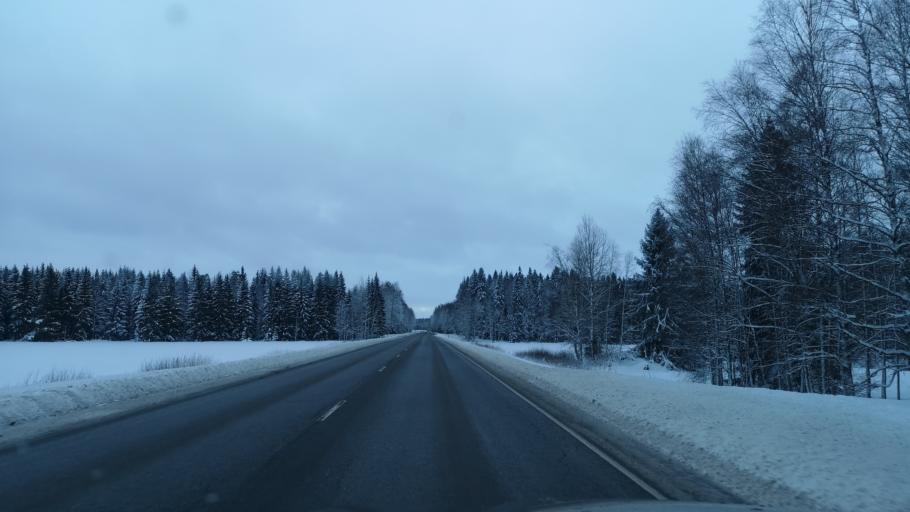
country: FI
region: Varsinais-Suomi
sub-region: Loimaa
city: Loimaa
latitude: 60.9128
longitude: 23.1775
